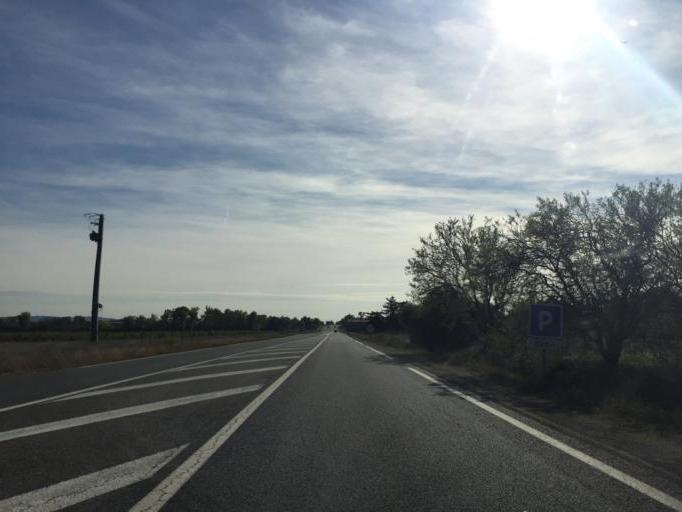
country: FR
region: Rhone-Alpes
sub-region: Departement de la Drome
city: Donzere
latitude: 44.4191
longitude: 4.7116
